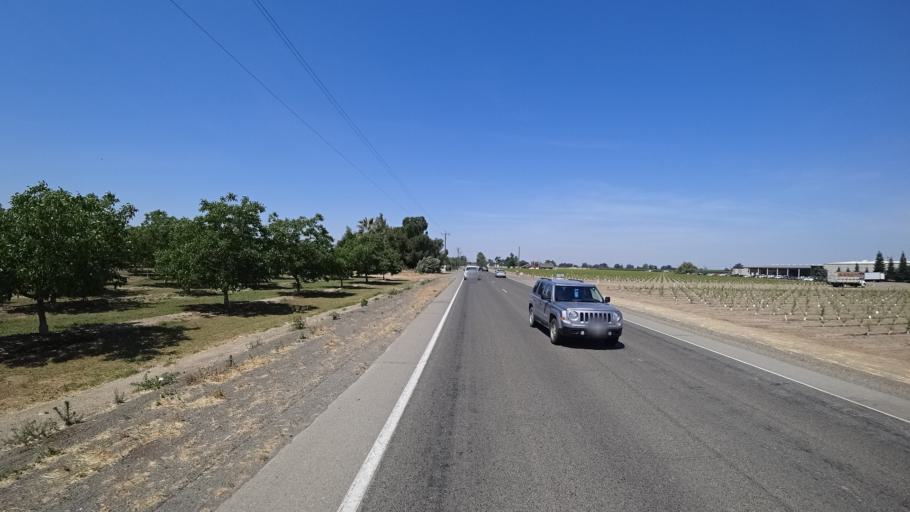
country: US
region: California
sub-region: Fresno County
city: Laton
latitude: 36.4010
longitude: -119.7394
